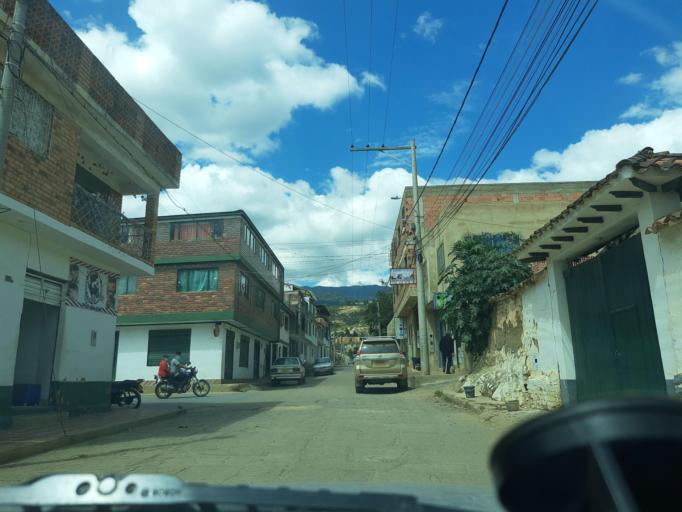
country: CO
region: Boyaca
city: Sutamarchan
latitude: 5.6214
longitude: -73.6212
